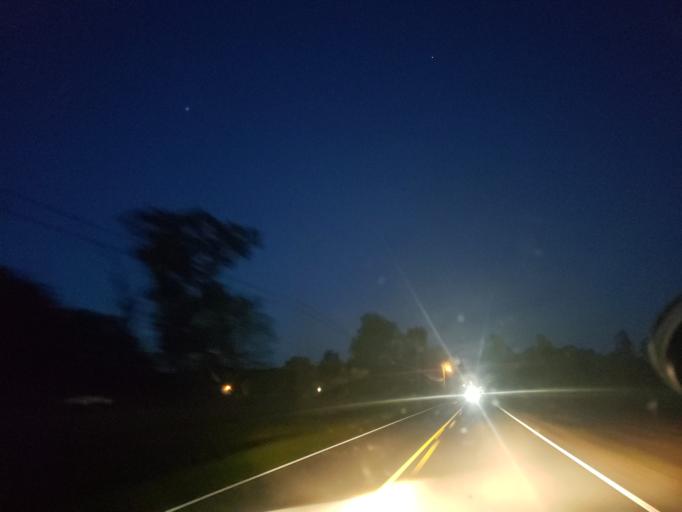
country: US
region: Alabama
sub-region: Madison County
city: Hazel Green
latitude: 34.9769
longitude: -86.6377
